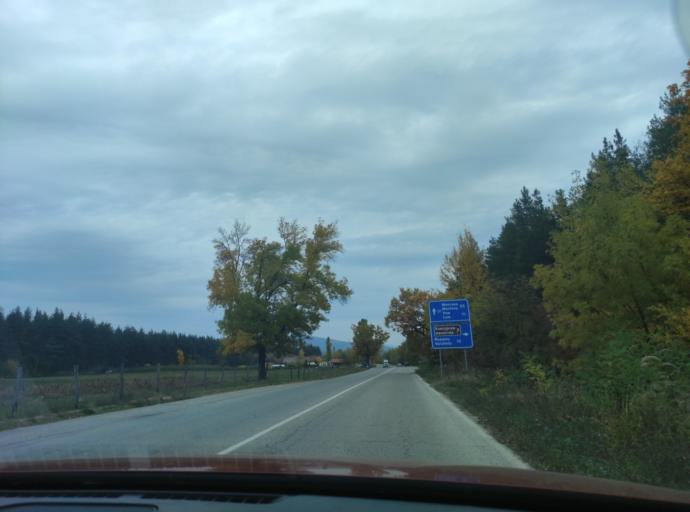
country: BG
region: Montana
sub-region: Obshtina Berkovitsa
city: Berkovitsa
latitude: 43.2170
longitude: 23.1595
